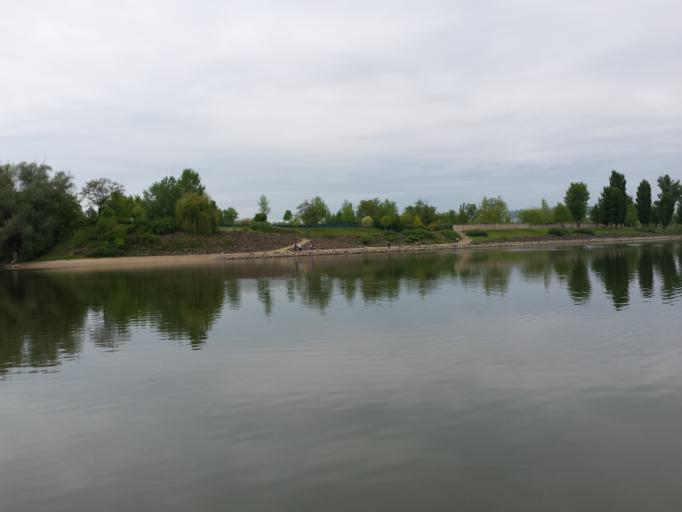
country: HU
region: Budapest
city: Budapest IX. keruelet
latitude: 47.4626
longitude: 19.0605
